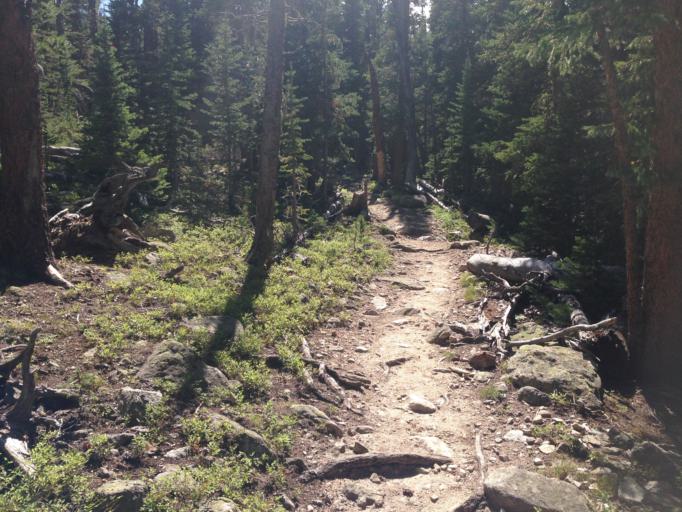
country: US
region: Colorado
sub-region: Larimer County
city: Estes Park
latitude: 40.1903
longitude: -105.5835
